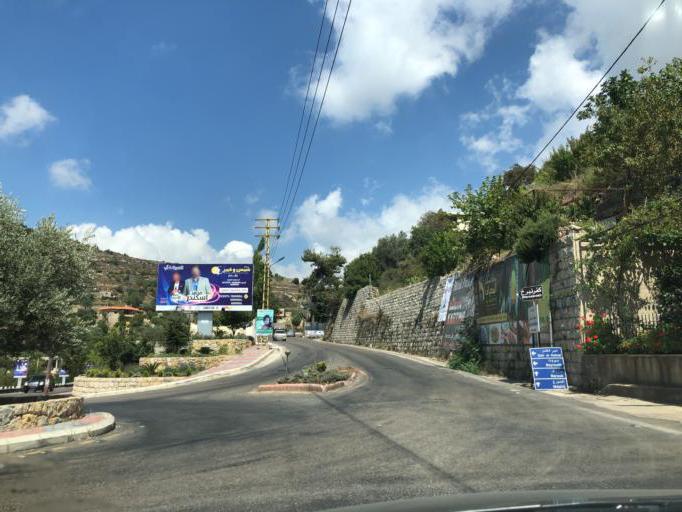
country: LB
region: Mont-Liban
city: Beit ed Dine
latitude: 33.6989
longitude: 35.5977
